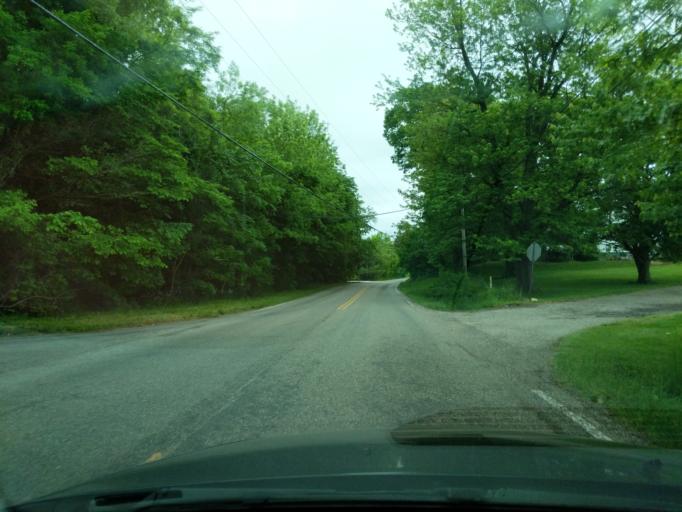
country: US
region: Ohio
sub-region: Stark County
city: Massillon
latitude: 40.7782
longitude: -81.5706
